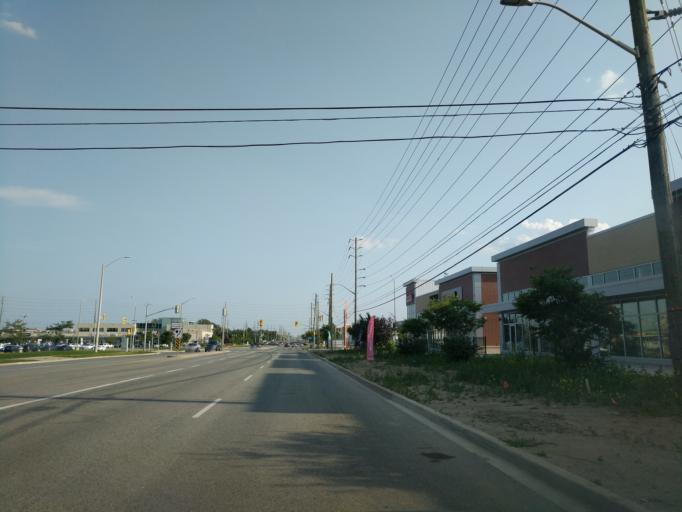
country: CA
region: Ontario
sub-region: York
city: Richmond Hill
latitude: 43.8524
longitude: -79.3588
